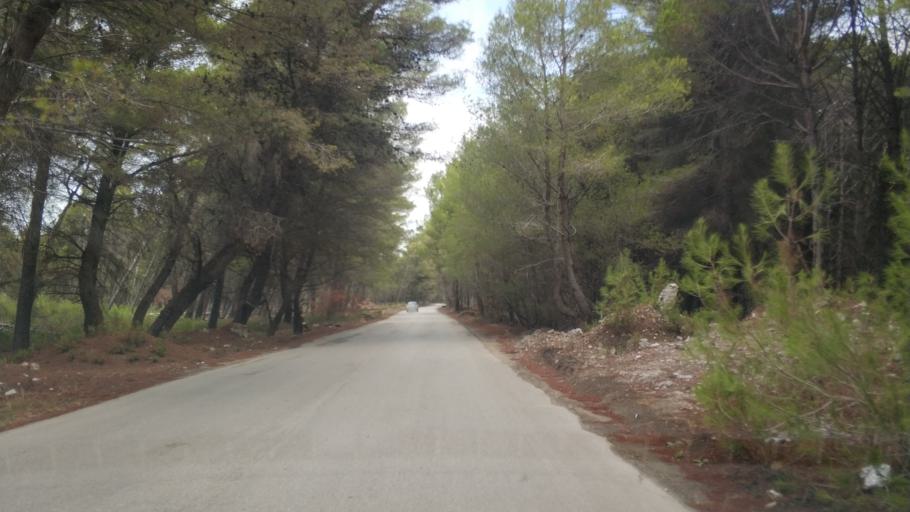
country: AL
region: Vlore
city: Vlore
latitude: 40.4824
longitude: 19.4481
